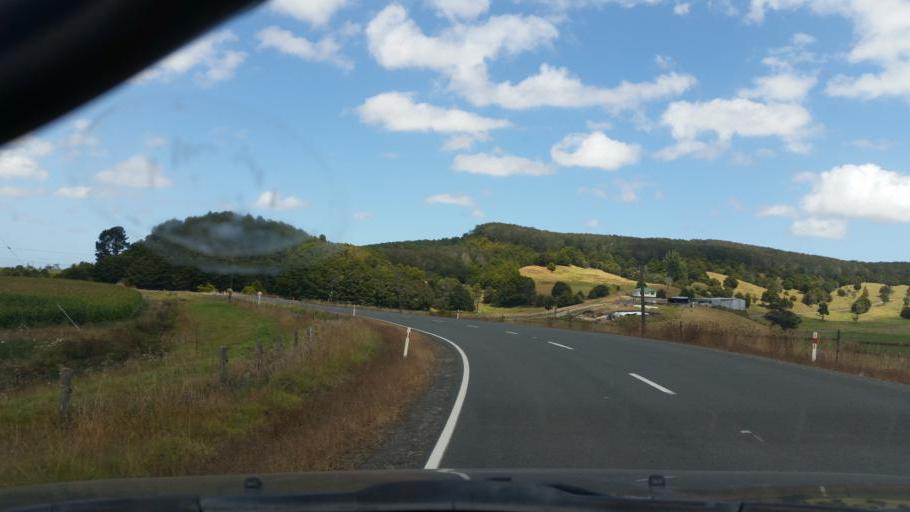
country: NZ
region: Northland
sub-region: Kaipara District
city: Dargaville
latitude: -35.8632
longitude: 173.8432
